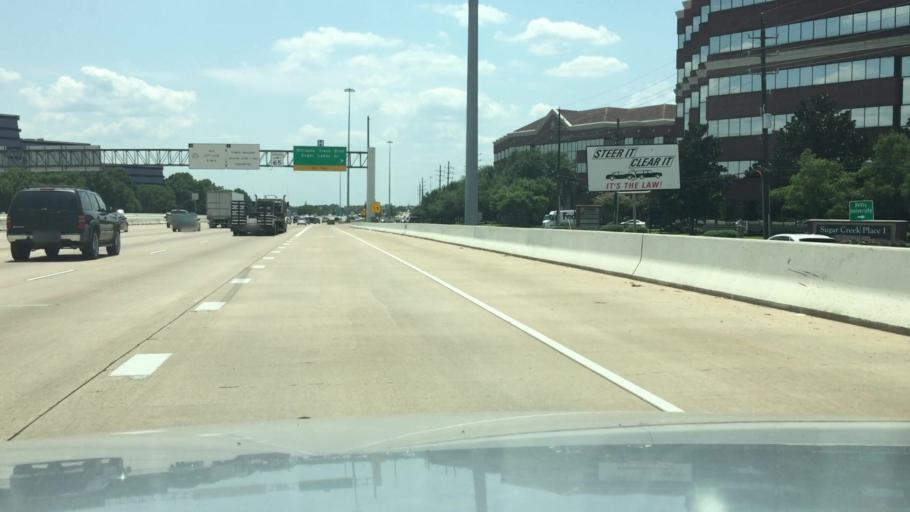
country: US
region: Texas
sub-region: Fort Bend County
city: Sugar Land
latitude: 29.6176
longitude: -95.6053
